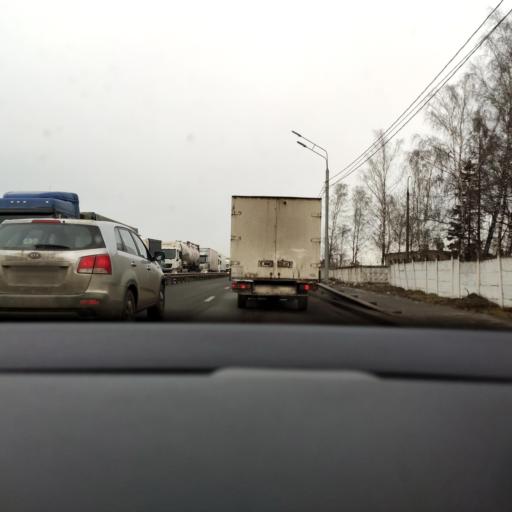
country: RU
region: Moskovskaya
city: Bol'shiye Vyazemy
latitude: 55.6318
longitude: 37.0047
